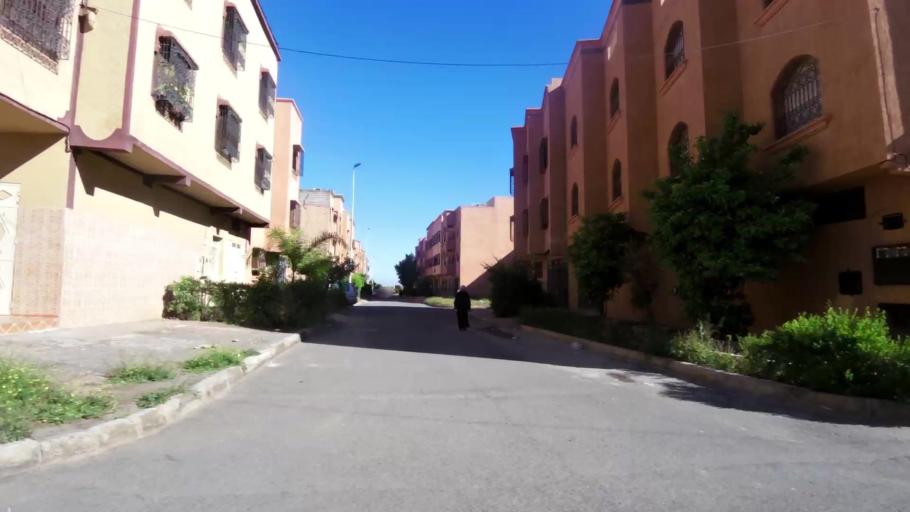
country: MA
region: Marrakech-Tensift-Al Haouz
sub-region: Marrakech
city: Marrakesh
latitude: 31.6002
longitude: -8.0405
